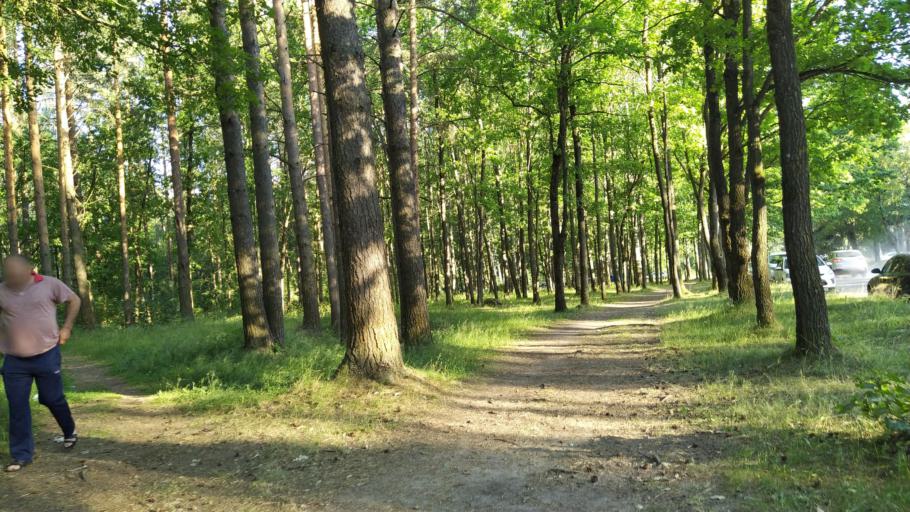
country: RU
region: Leningrad
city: Koltushi
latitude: 59.9181
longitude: 30.7353
